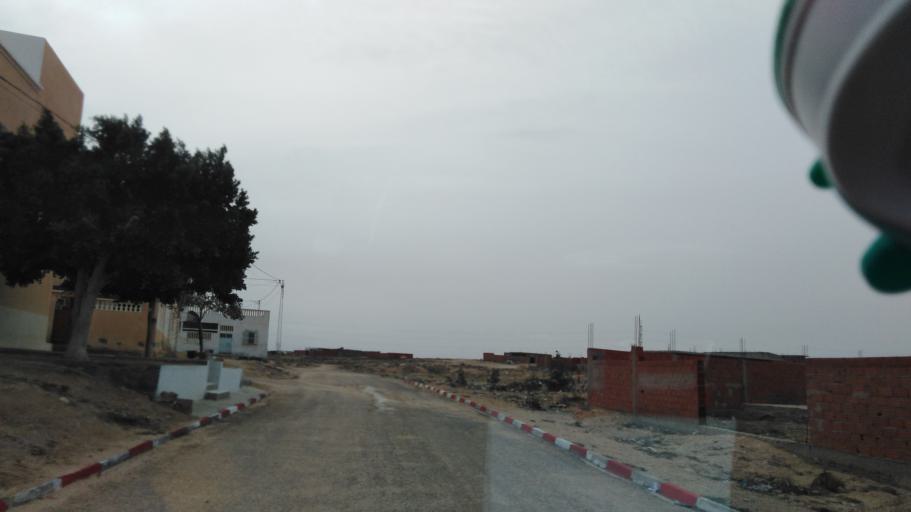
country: TN
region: Qabis
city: Gabes
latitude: 33.9497
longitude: 10.0023
